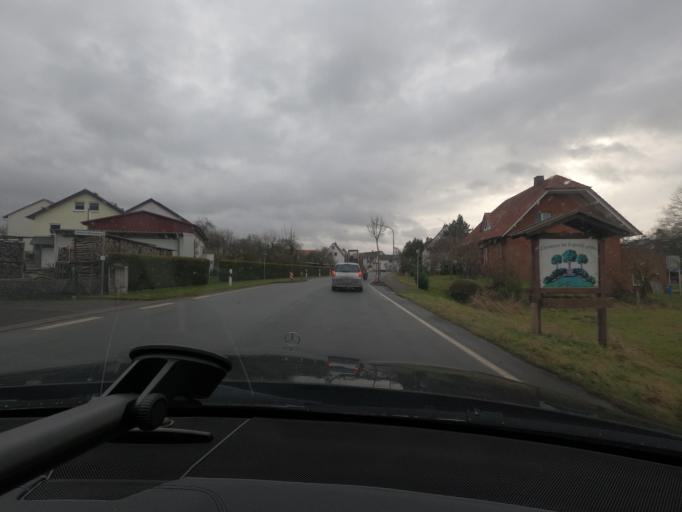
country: DE
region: Hesse
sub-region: Regierungsbezirk Kassel
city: Volkmarsen
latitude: 51.3869
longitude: 9.1444
